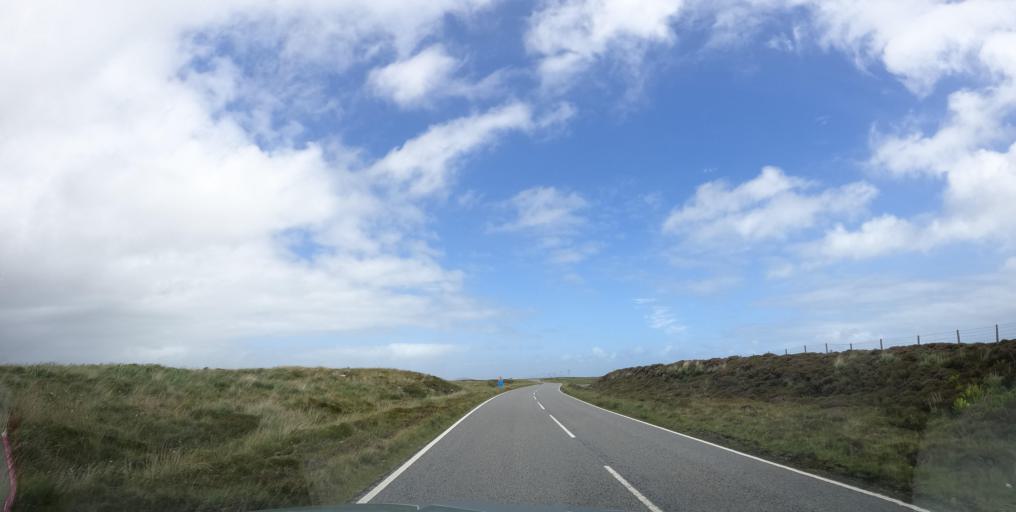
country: GB
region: Scotland
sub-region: Eilean Siar
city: Benbecula
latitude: 57.3640
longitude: -7.3540
